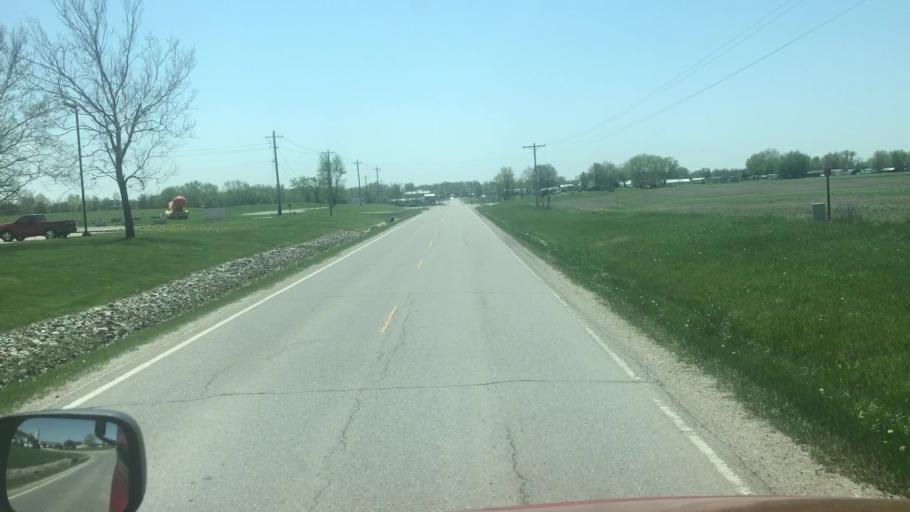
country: US
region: Missouri
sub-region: Adair County
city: Kirksville
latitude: 40.2195
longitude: -92.5923
